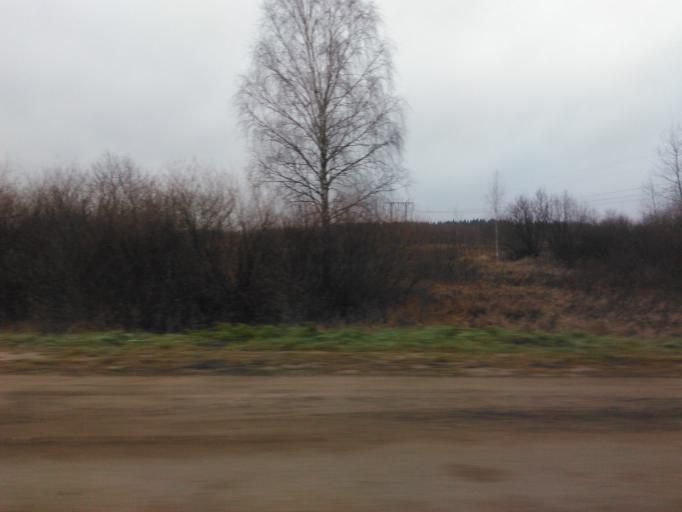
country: RU
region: Moskovskaya
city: Ashukino
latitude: 56.1356
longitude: 37.9823
